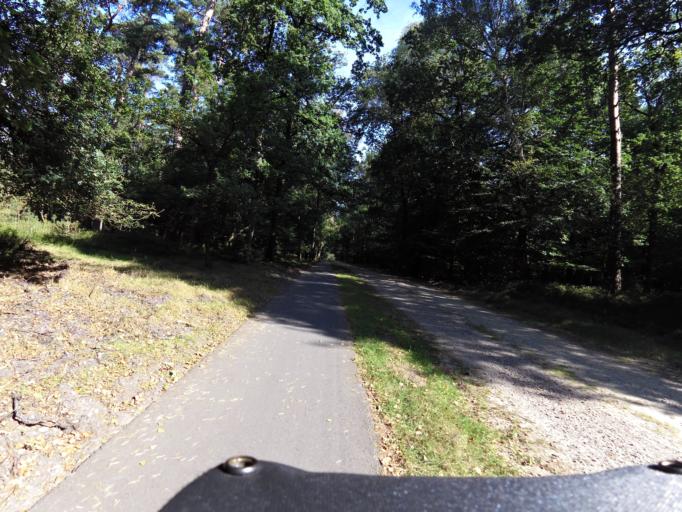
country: NL
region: Gelderland
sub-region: Gemeente Apeldoorn
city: Apeldoorn
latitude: 52.1970
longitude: 5.8847
